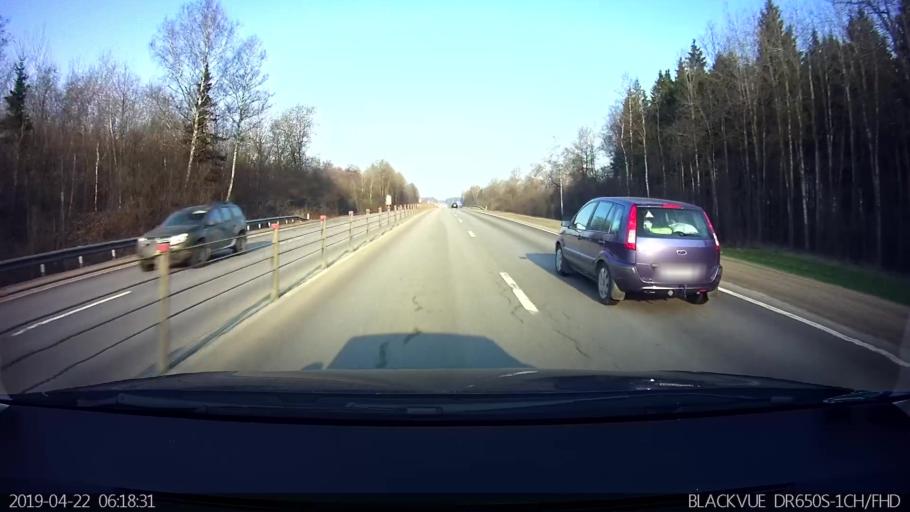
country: RU
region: Moskovskaya
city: Mozhaysk
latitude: 55.4634
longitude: 35.9562
